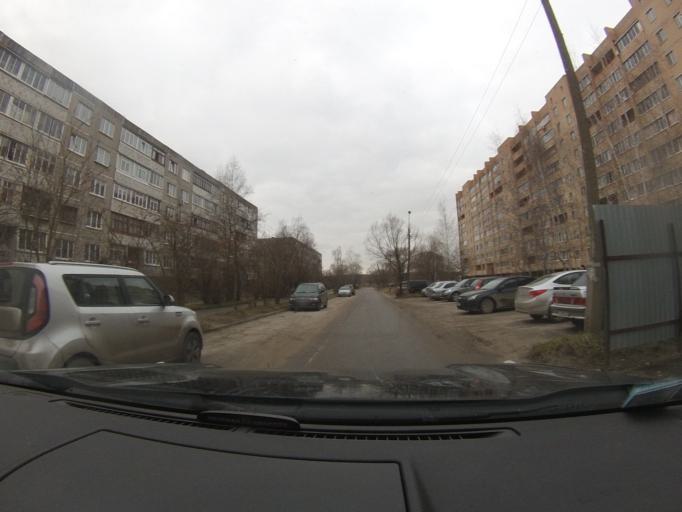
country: RU
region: Moskovskaya
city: Lopatinskiy
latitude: 55.3412
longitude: 38.7156
